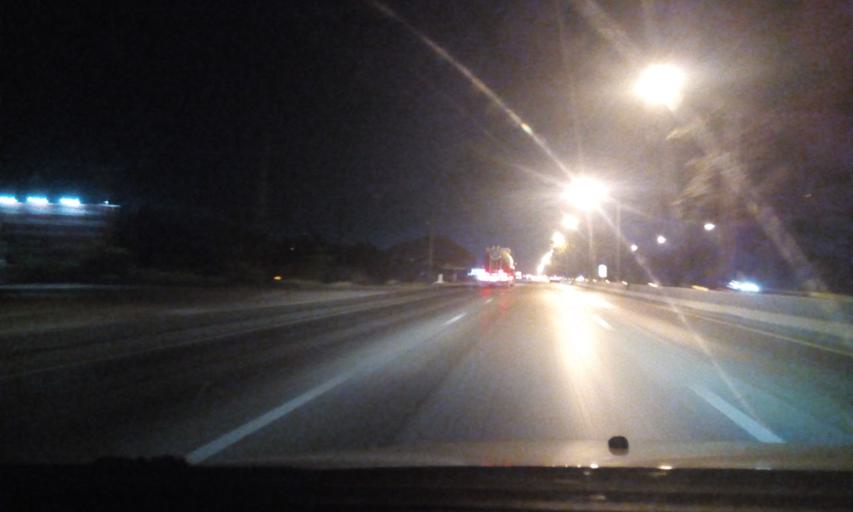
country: TH
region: Sing Buri
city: Phrom Buri
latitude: 14.7637
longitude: 100.4517
